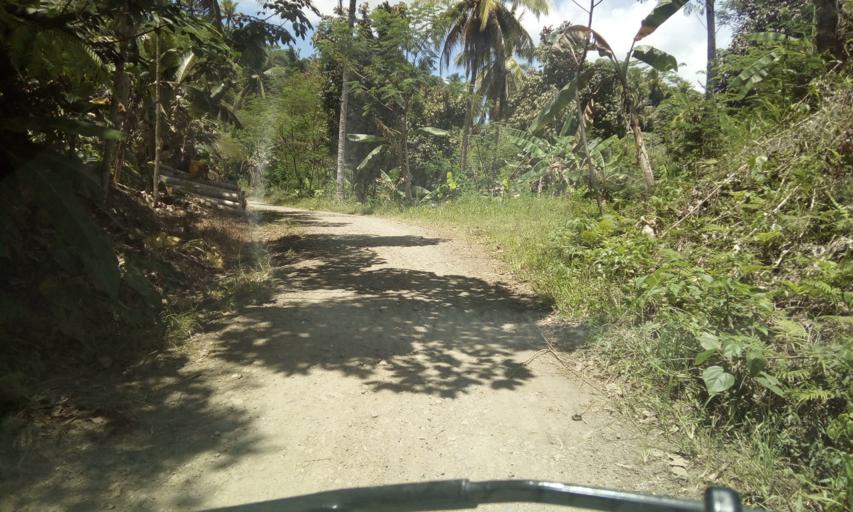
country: PH
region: Caraga
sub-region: Province of Agusan del Sur
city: Santa Josefa
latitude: 7.9544
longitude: 125.9935
